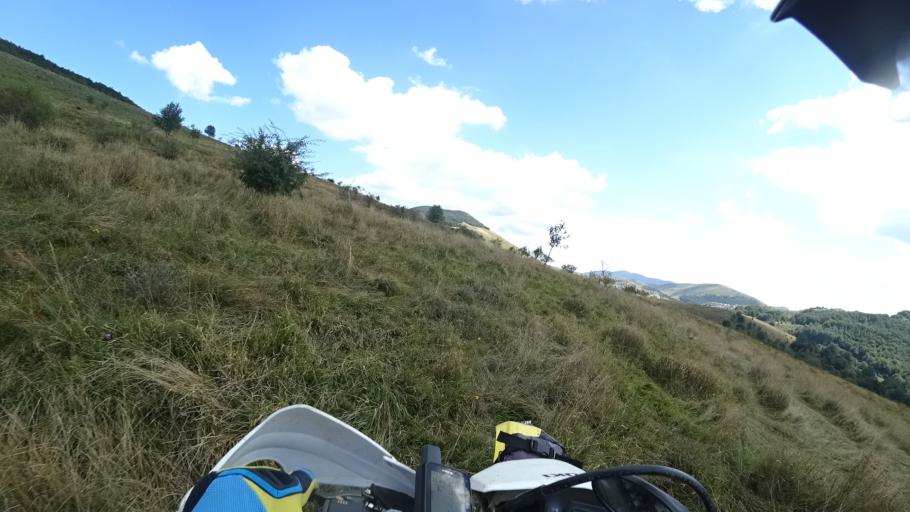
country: HR
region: Zadarska
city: Gracac
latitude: 44.4215
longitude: 15.9968
